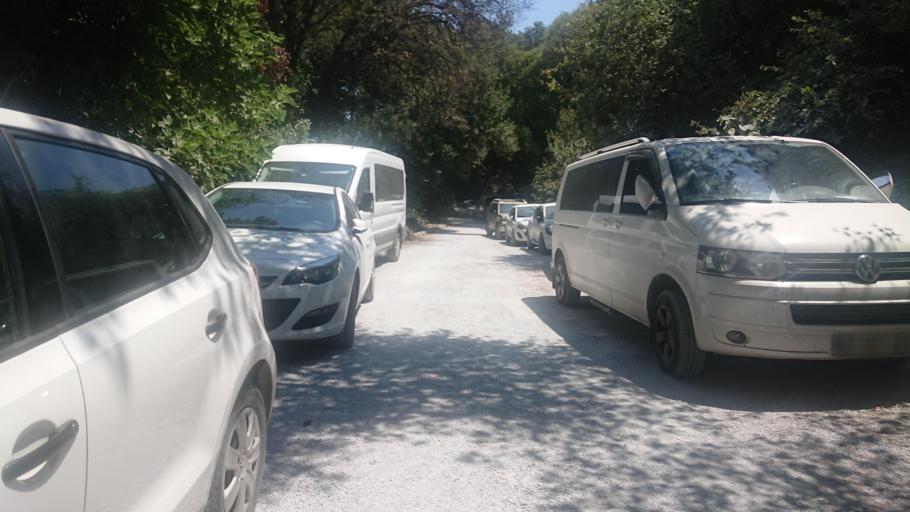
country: TR
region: Aydin
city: Atburgazi
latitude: 37.6922
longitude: 27.1501
